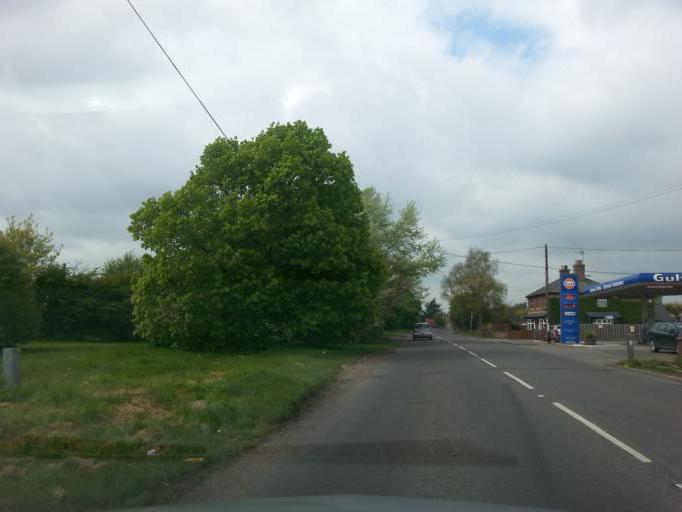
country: GB
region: England
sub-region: Norfolk
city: Outwell
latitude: 52.6181
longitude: 0.2300
